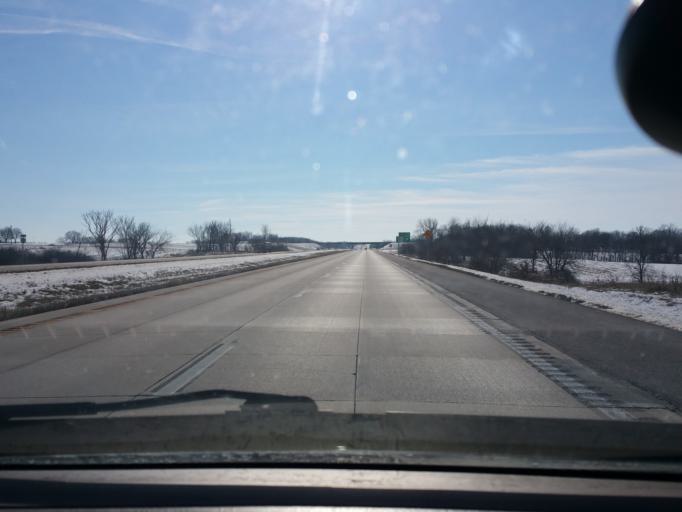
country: US
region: Missouri
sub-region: Daviess County
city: Gallatin
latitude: 40.0032
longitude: -94.0964
